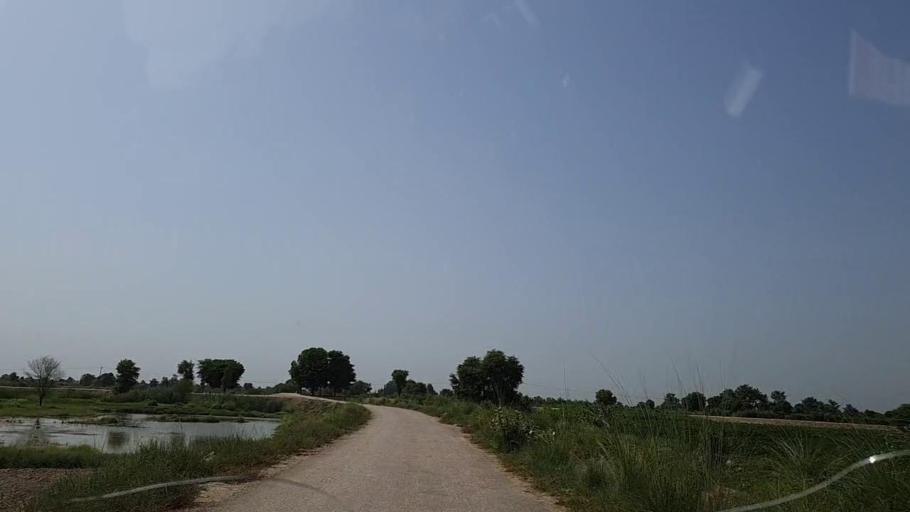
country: PK
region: Sindh
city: Kandiaro
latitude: 27.0487
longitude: 68.1646
